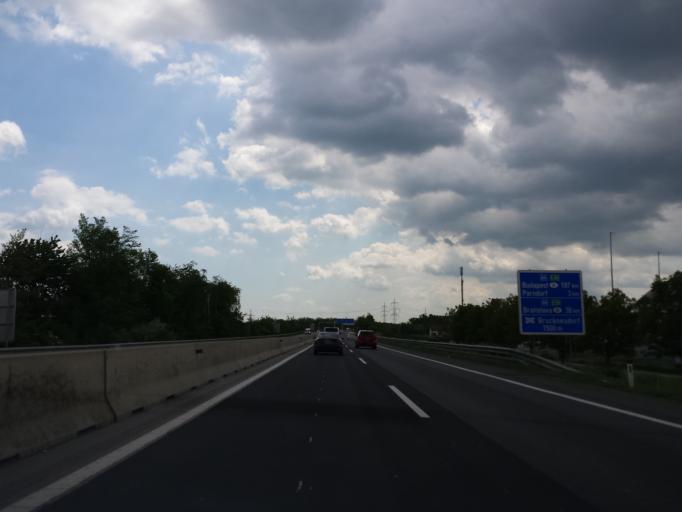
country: AT
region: Burgenland
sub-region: Politischer Bezirk Neusiedl am See
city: Bruckneudorf
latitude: 48.0339
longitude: 16.8206
